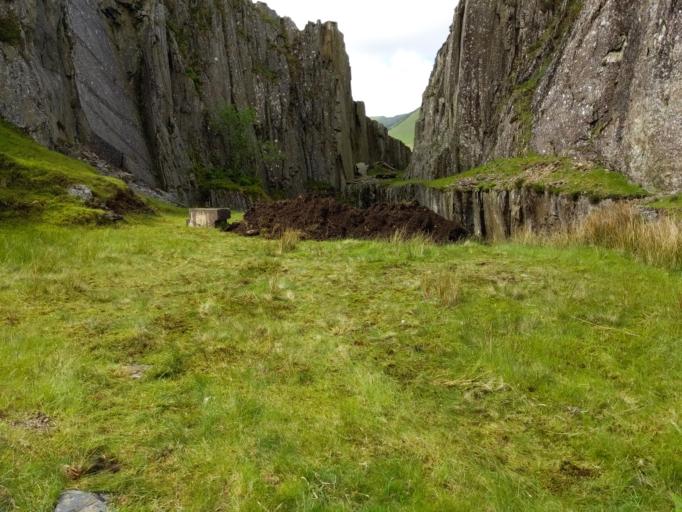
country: GB
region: Wales
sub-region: Gwynedd
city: Llanberis
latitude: 53.0517
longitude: -4.1296
